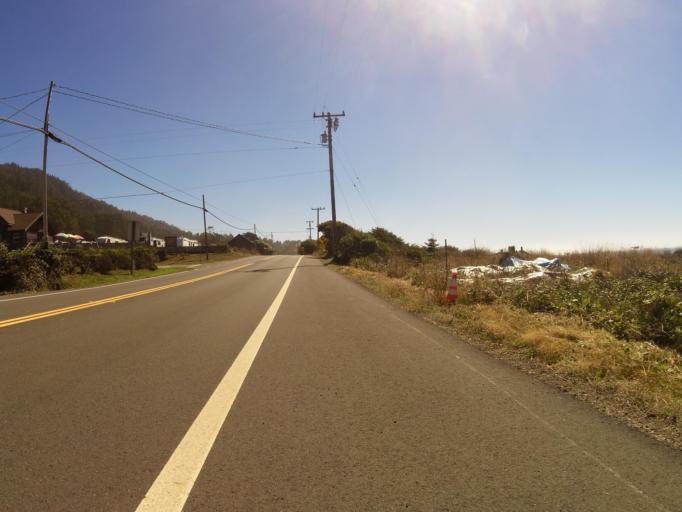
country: US
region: California
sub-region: Mendocino County
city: Fort Bragg
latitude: 39.6371
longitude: -123.7850
